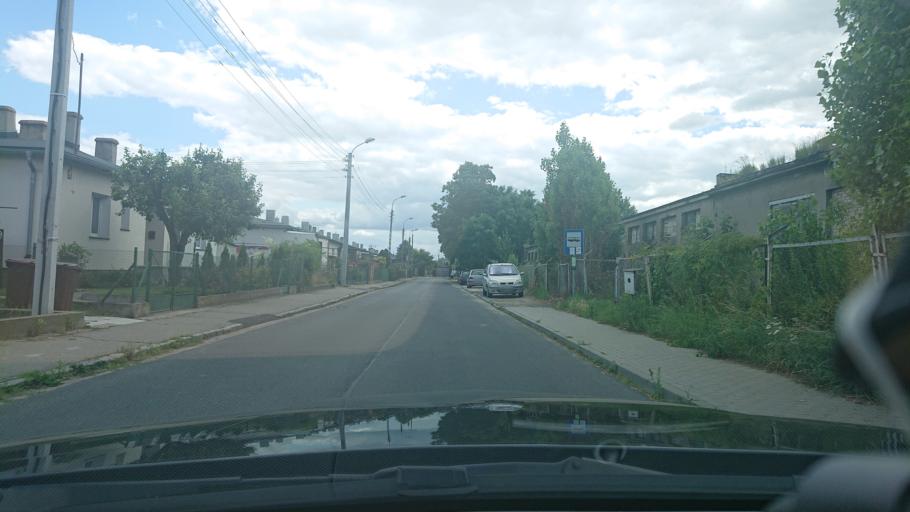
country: PL
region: Greater Poland Voivodeship
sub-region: Powiat gnieznienski
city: Gniezno
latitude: 52.5163
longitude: 17.6052
